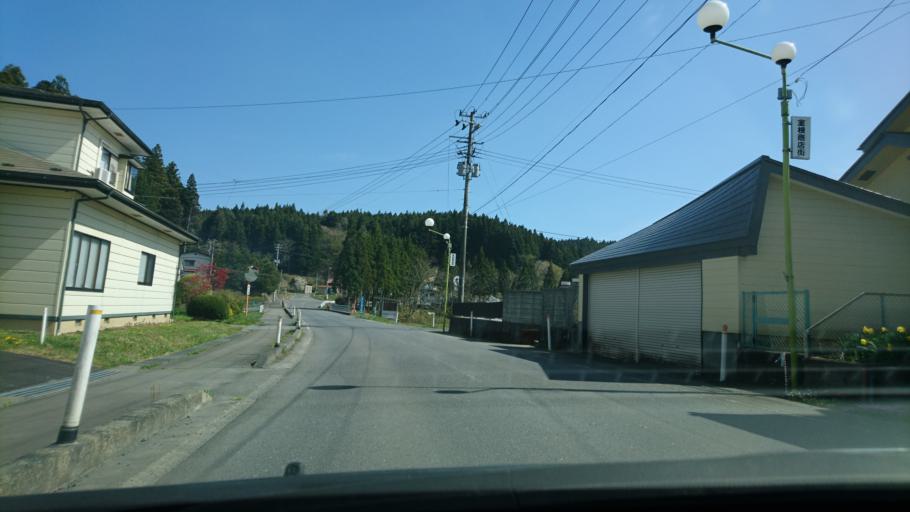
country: JP
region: Iwate
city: Ofunato
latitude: 38.9376
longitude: 141.4492
